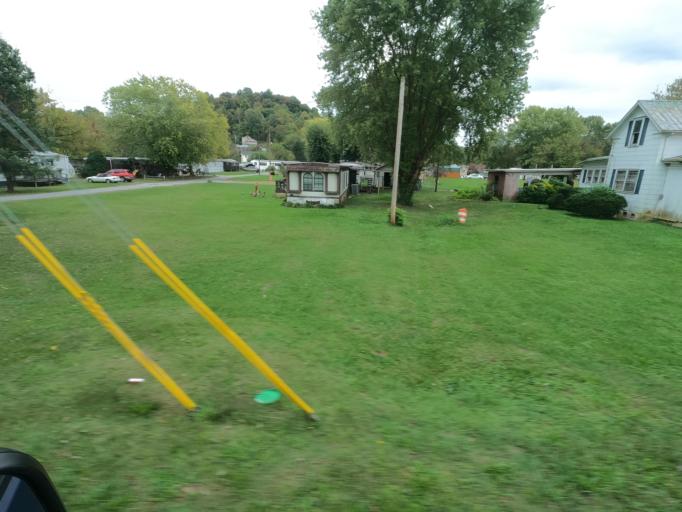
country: US
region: Tennessee
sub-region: Carter County
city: Central
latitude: 36.3322
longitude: -82.2632
